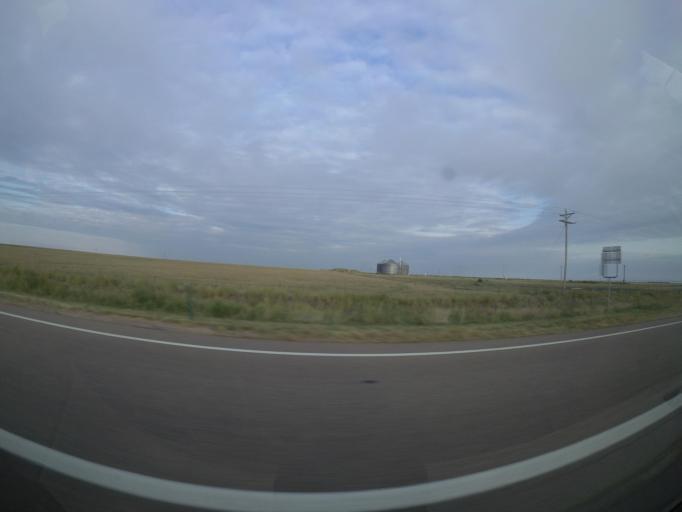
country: US
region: Colorado
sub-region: Yuma County
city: Wray
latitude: 39.7035
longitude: -102.2534
